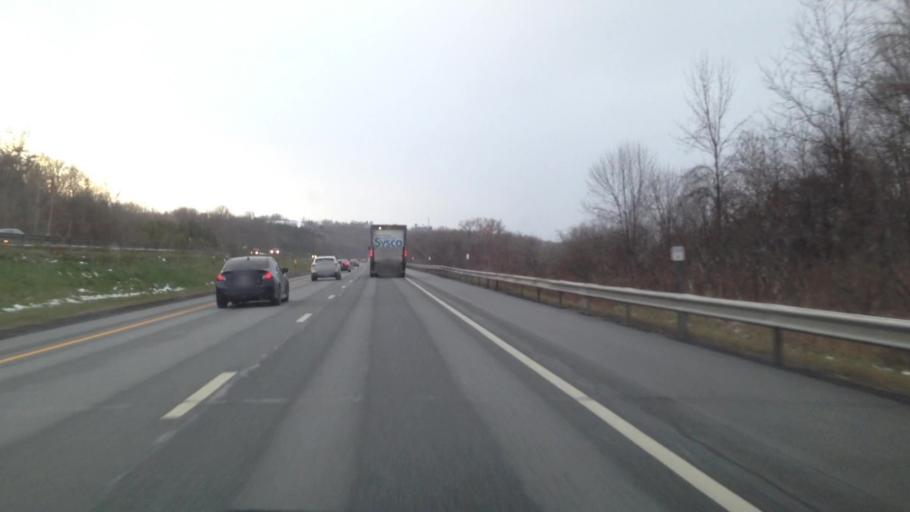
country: US
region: New York
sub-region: Montgomery County
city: Saint Johnsville
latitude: 42.9903
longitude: -74.7036
